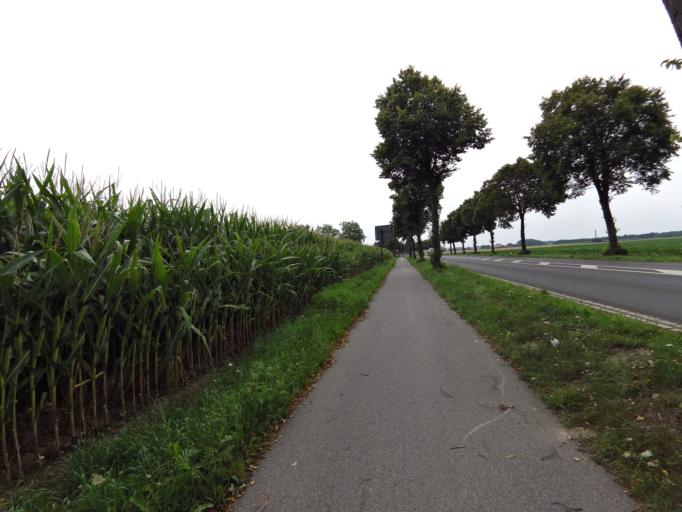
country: DE
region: North Rhine-Westphalia
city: Geilenkirchen
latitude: 50.9964
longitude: 6.1195
